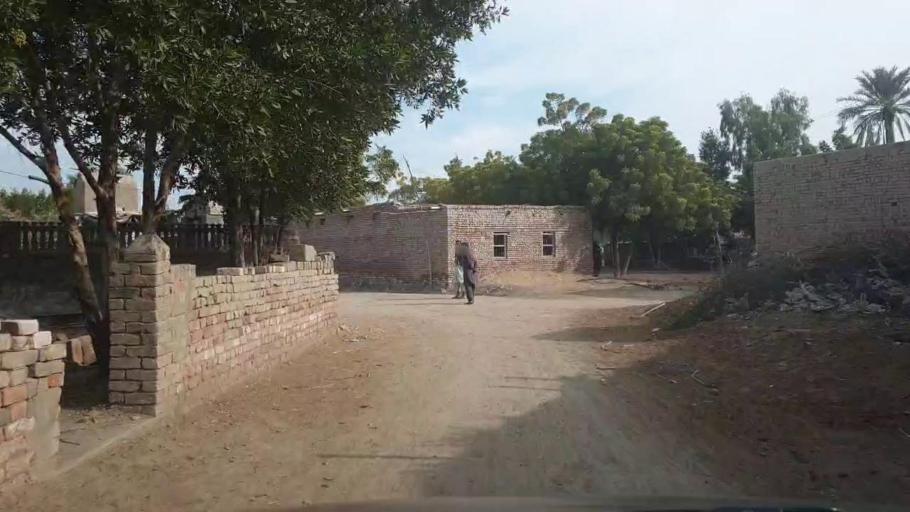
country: PK
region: Sindh
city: Khadro
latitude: 26.1592
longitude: 68.6959
